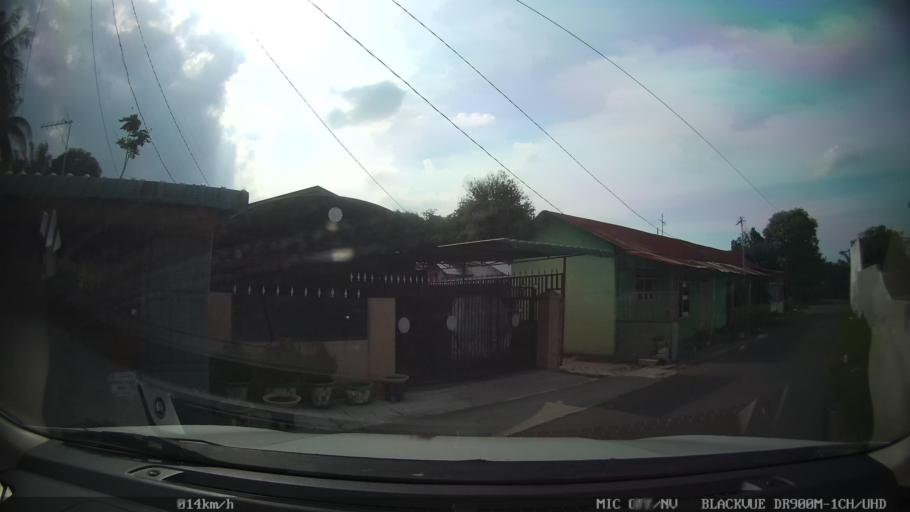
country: ID
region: North Sumatra
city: Binjai
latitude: 3.6034
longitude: 98.4930
